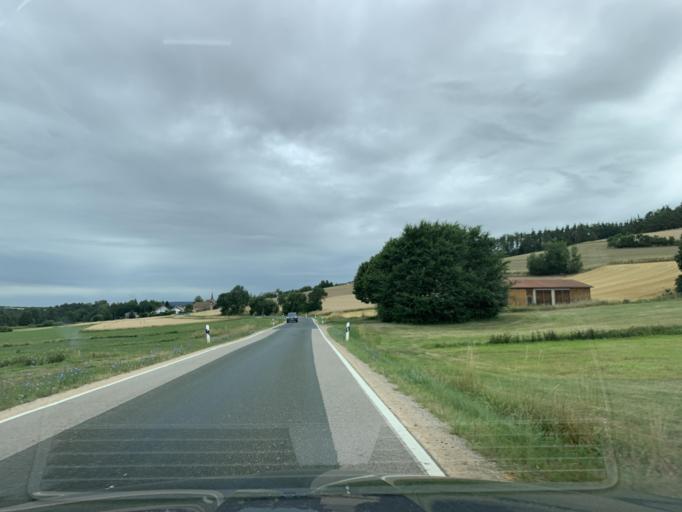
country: DE
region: Bavaria
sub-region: Upper Palatinate
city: Schwarzhofen
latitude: 49.3695
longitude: 12.3510
